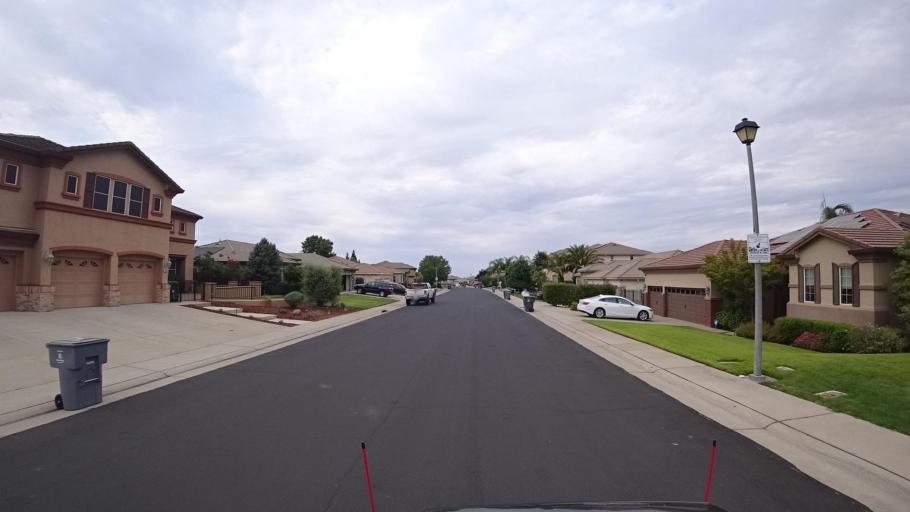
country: US
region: California
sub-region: Placer County
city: Rocklin
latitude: 38.7731
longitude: -121.2271
